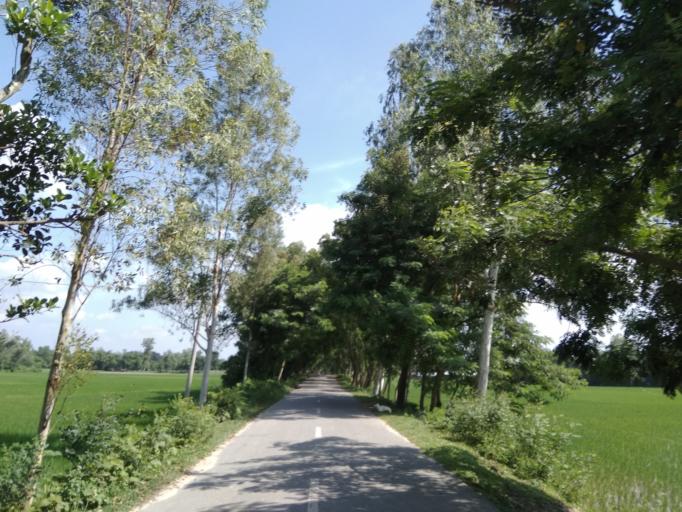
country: IN
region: West Bengal
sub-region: Koch Bihar
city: Haldibari
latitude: 26.1963
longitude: 88.6889
